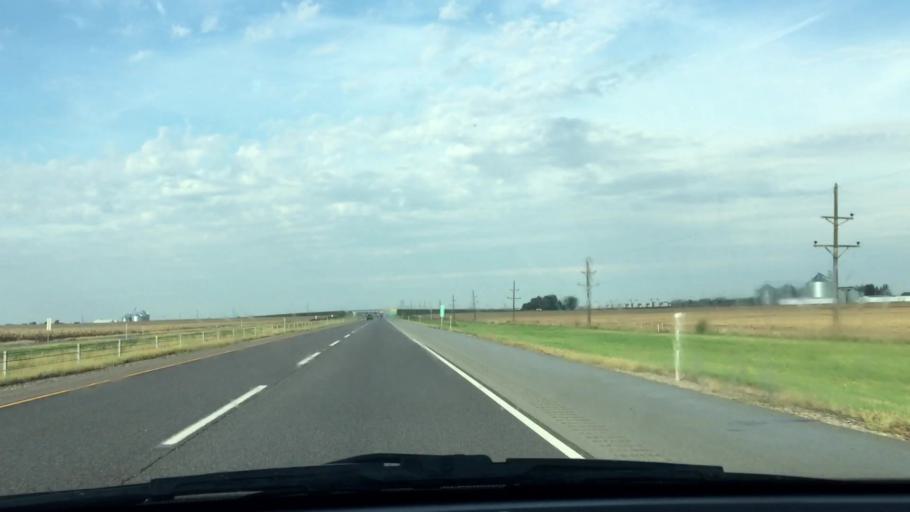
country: US
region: Illinois
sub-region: Lee County
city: Franklin Grove
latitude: 41.8229
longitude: -89.3757
